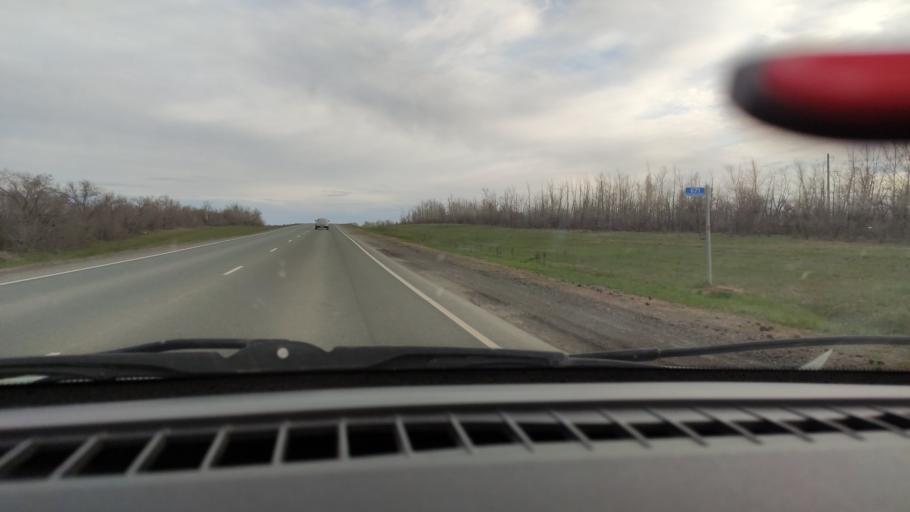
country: RU
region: Orenburg
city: Sakmara
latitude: 52.1616
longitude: 55.2889
